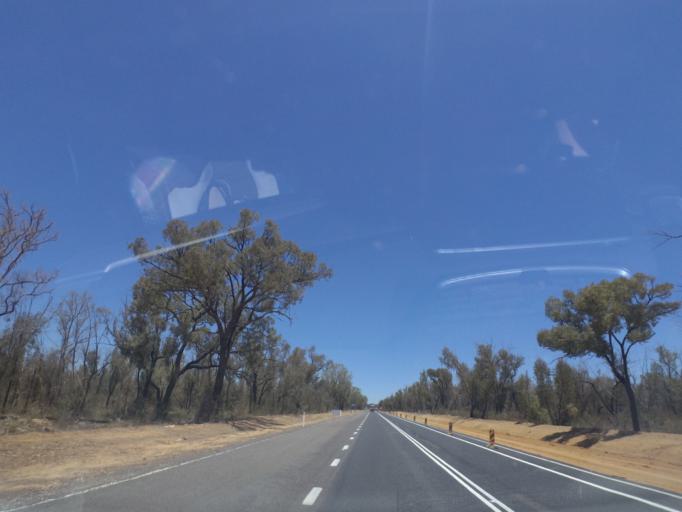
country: AU
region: New South Wales
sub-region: Warrumbungle Shire
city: Coonabarabran
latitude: -30.9356
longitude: 149.4264
